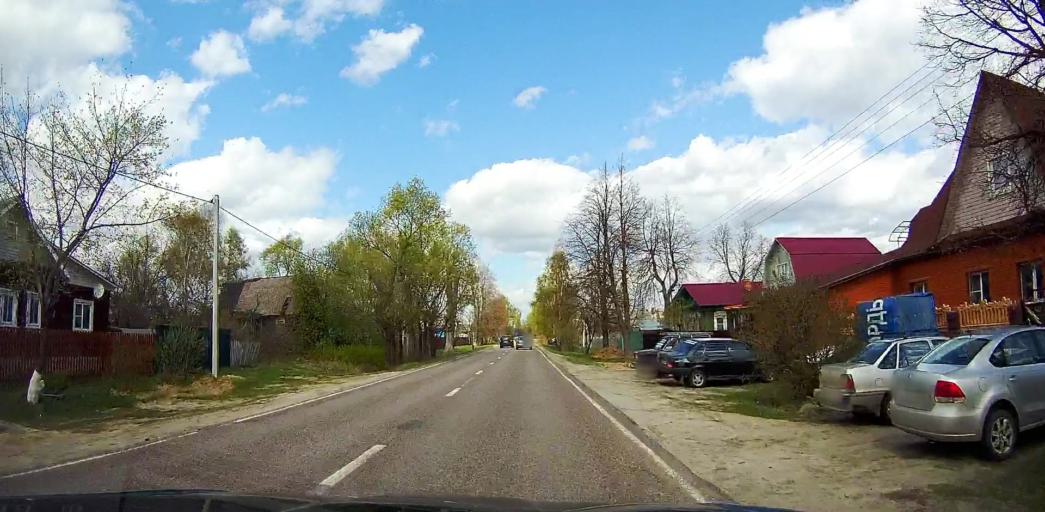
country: RU
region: Moskovskaya
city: Davydovo
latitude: 55.5780
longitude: 38.8227
